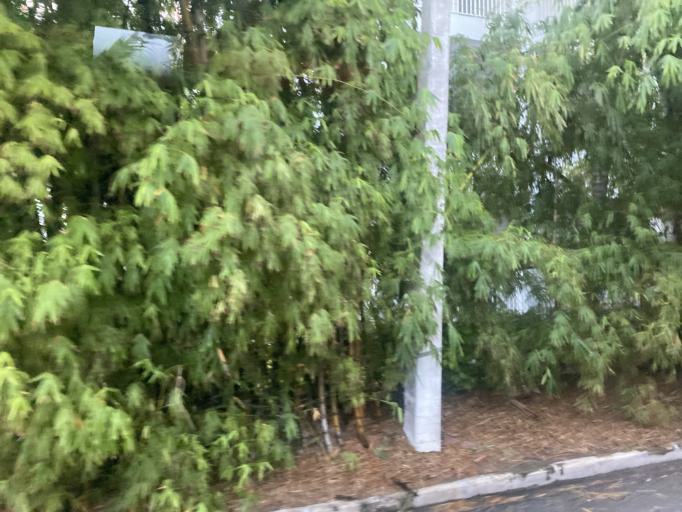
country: DO
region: San Juan
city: Punta Cana
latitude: 18.7212
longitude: -68.4589
